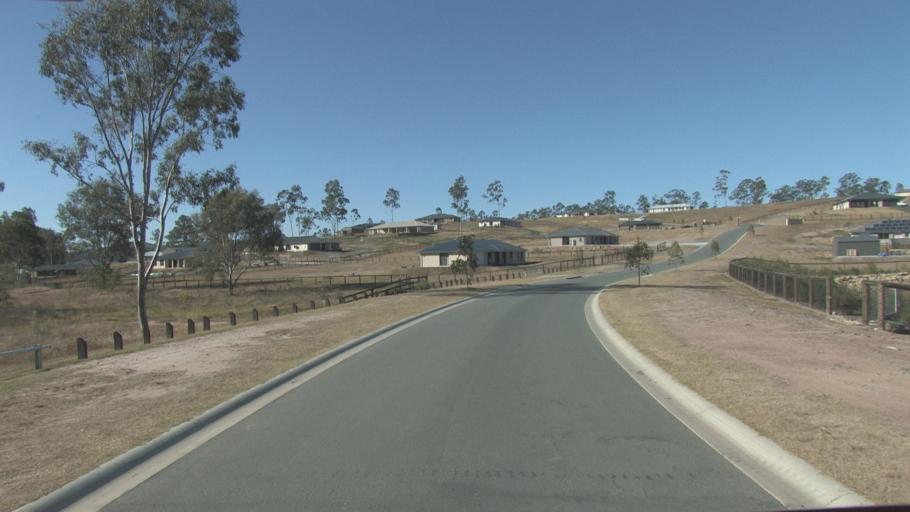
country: AU
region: Queensland
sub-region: Logan
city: Cedar Vale
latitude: -27.8734
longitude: 153.0482
